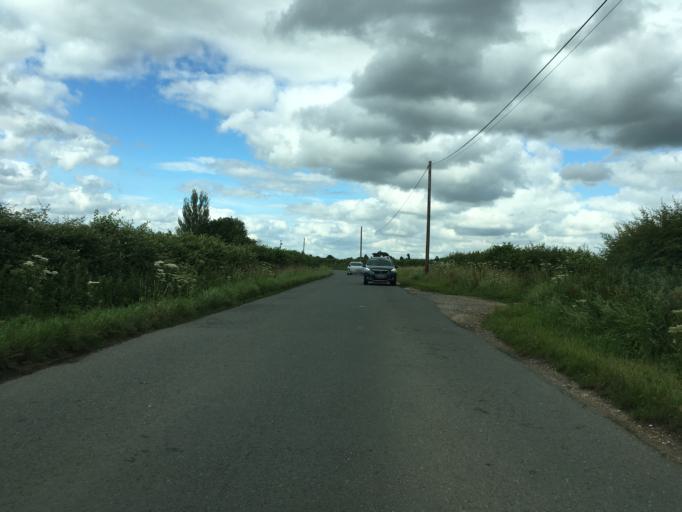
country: GB
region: England
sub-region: Gloucestershire
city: Stonehouse
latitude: 51.7933
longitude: -2.3530
